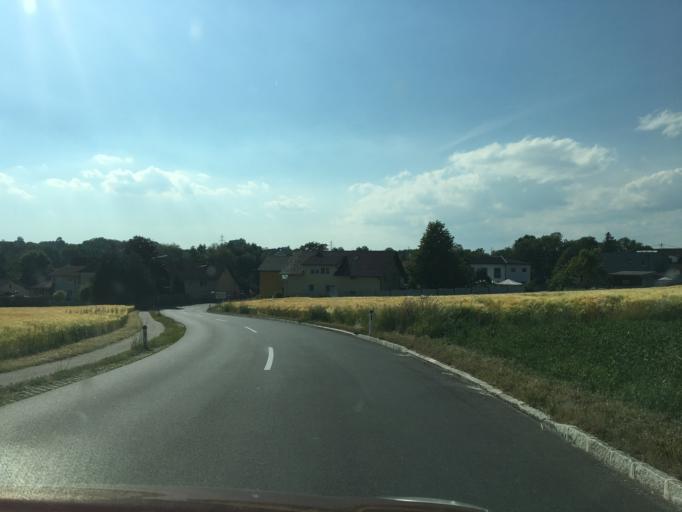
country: AT
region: Lower Austria
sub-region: Politischer Bezirk Amstetten
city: Ennsdorf
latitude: 48.2747
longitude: 14.5185
